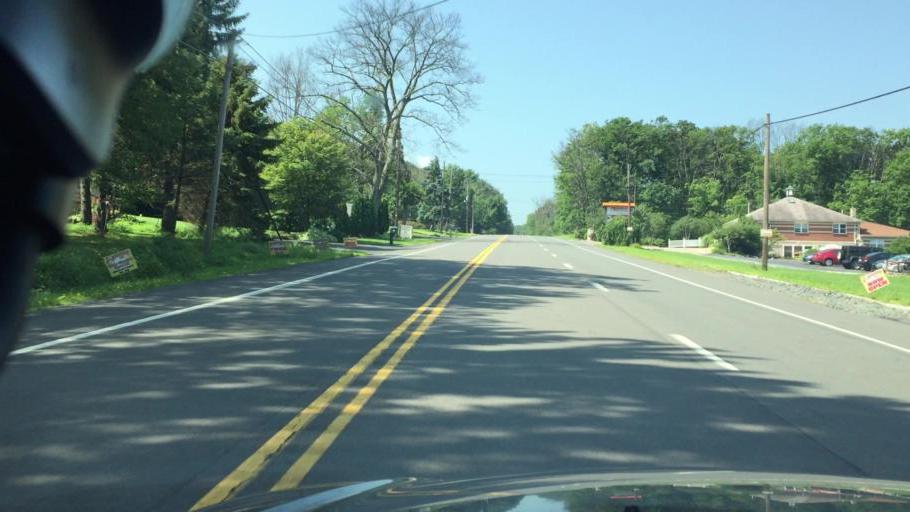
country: US
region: Pennsylvania
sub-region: Luzerne County
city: Freeland
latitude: 41.0924
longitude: -75.9371
